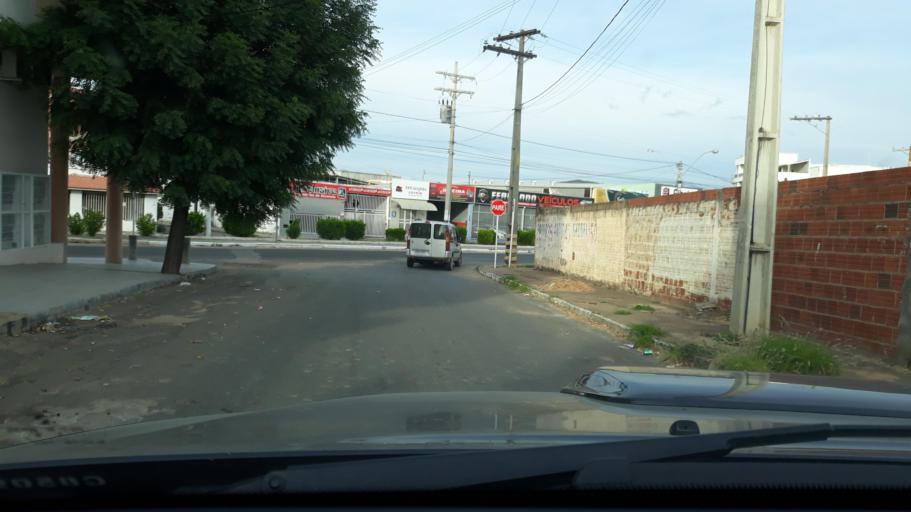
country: BR
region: Bahia
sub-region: Guanambi
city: Guanambi
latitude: -14.2307
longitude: -42.7786
